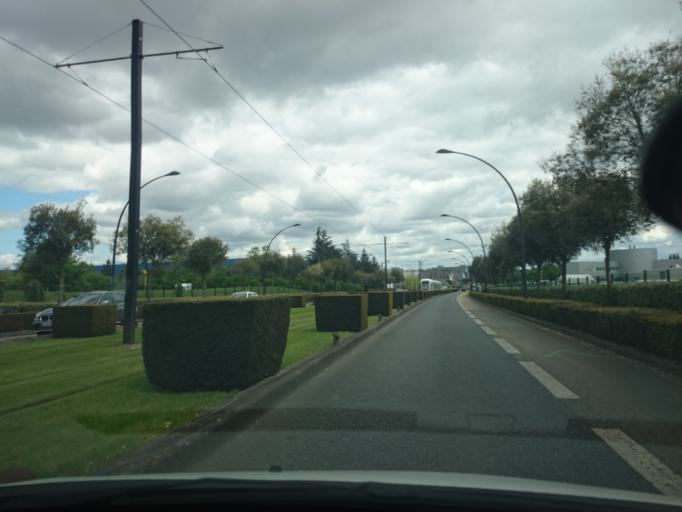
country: FR
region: Pays de la Loire
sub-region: Departement de la Loire-Atlantique
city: Saint-Herblain
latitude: 47.2218
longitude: -1.6359
